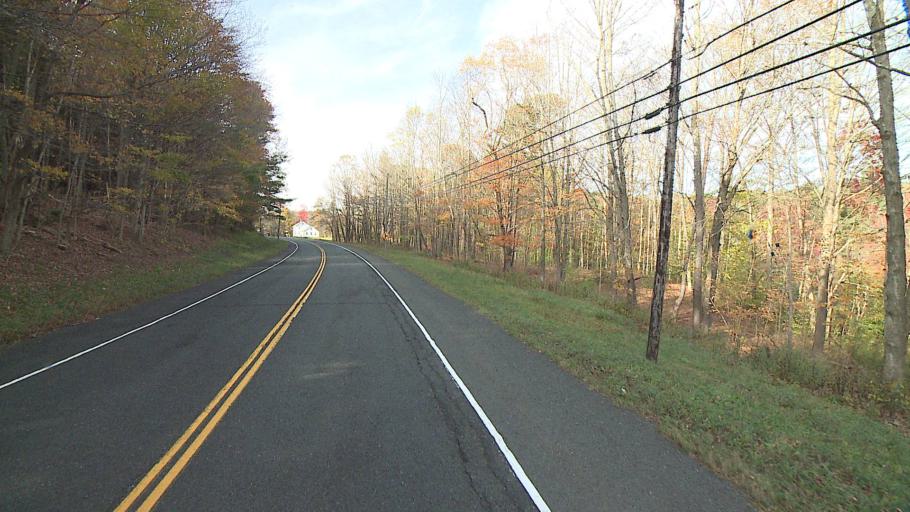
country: US
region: Connecticut
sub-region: Litchfield County
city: Winchester Center
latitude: 41.9591
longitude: -73.1190
